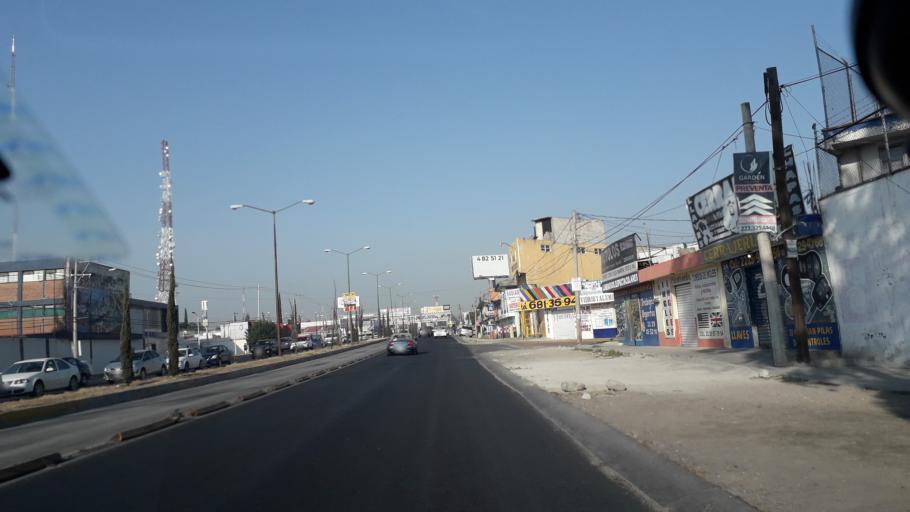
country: MX
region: Puebla
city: Tlazcalancingo
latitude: 19.0349
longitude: -98.2590
